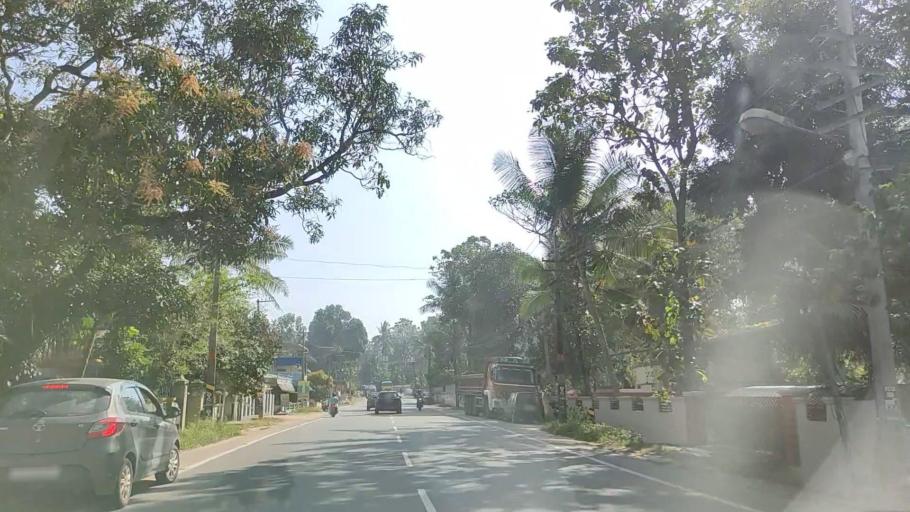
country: IN
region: Kerala
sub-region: Kollam
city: Punalur
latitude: 8.9328
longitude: 76.9379
